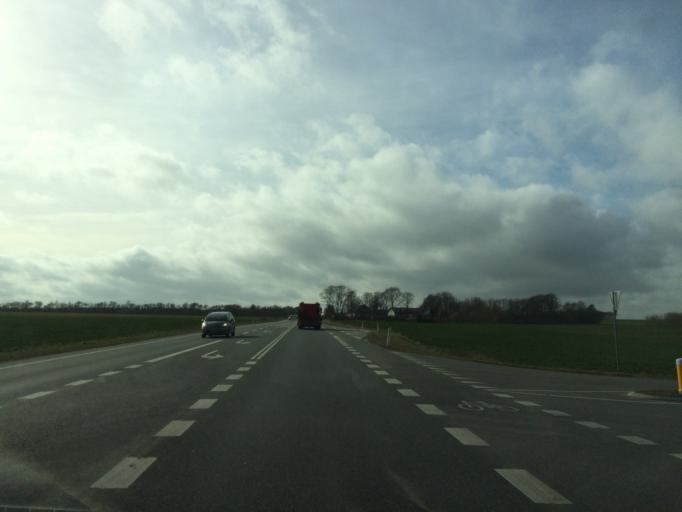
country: DK
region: Central Jutland
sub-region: Randers Kommune
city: Langa
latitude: 56.4738
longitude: 9.9385
